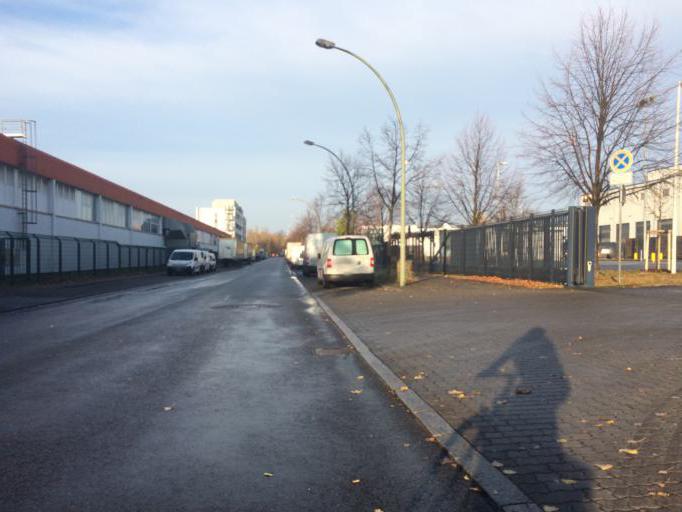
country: DE
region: Berlin
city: Wilhelmsruh
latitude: 52.5807
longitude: 13.3569
